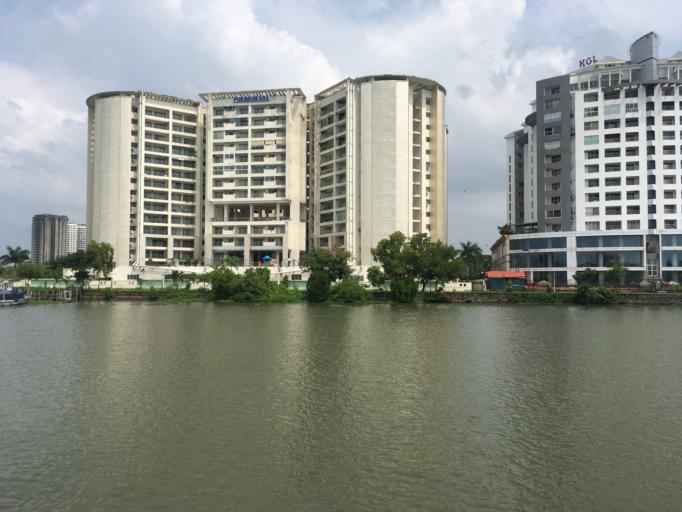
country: IN
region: Kerala
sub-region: Ernakulam
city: Cochin
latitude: 9.9891
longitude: 76.2692
